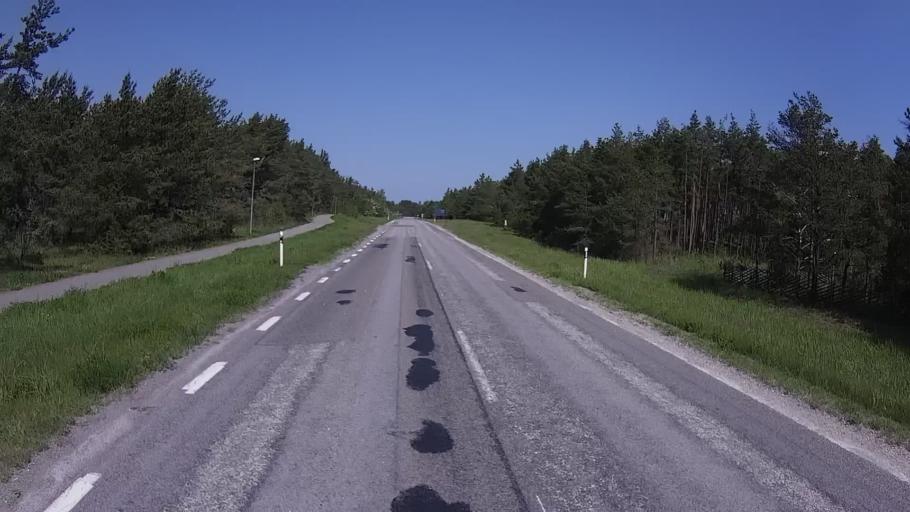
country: EE
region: Saare
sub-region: Kuressaare linn
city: Kuressaare
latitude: 58.1734
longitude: 22.2528
